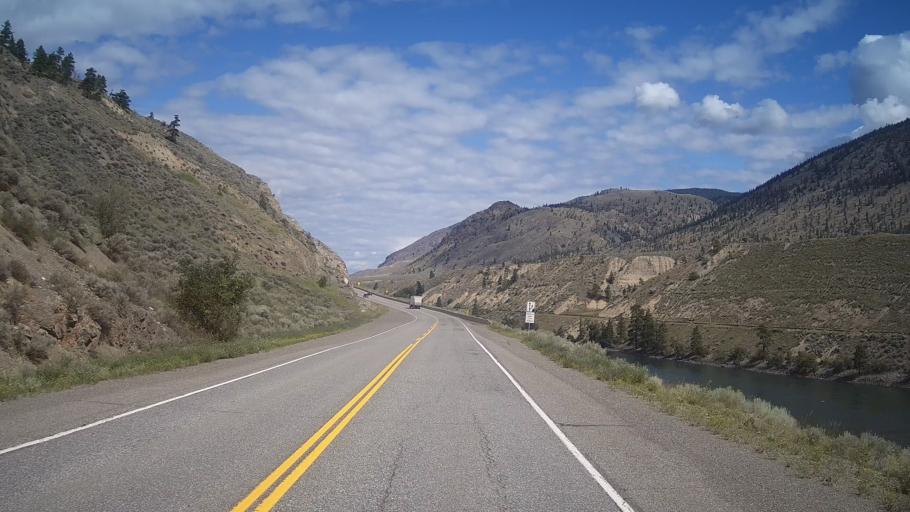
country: CA
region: British Columbia
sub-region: Thompson-Nicola Regional District
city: Ashcroft
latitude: 50.5326
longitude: -121.2857
